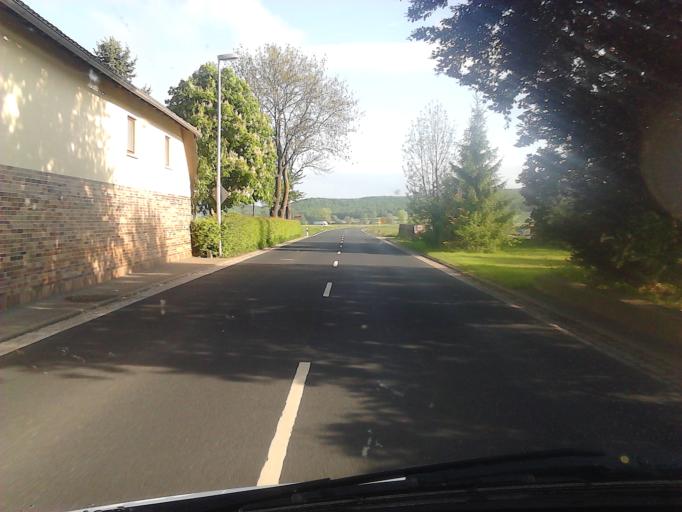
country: DE
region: Bavaria
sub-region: Regierungsbezirk Unterfranken
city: Bundorf
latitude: 50.2730
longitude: 10.5255
